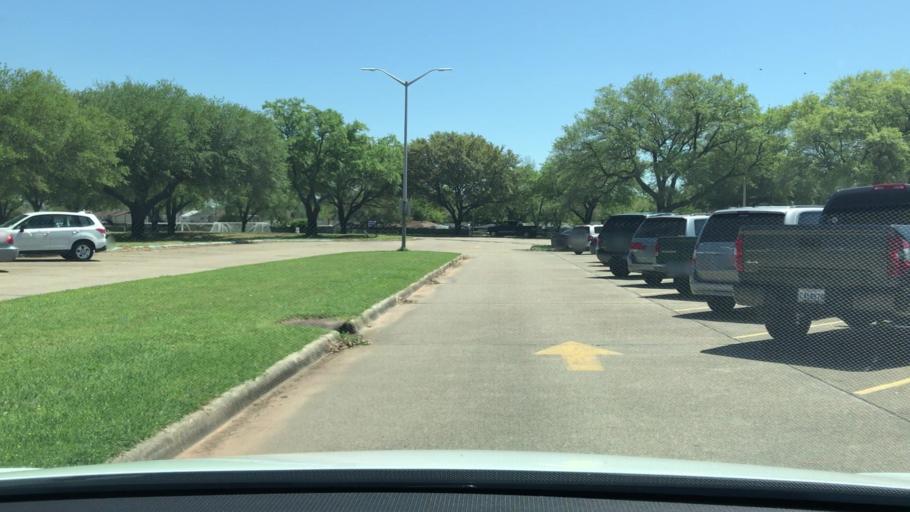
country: US
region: Louisiana
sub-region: Bossier Parish
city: Bossier City
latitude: 32.4270
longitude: -93.7037
